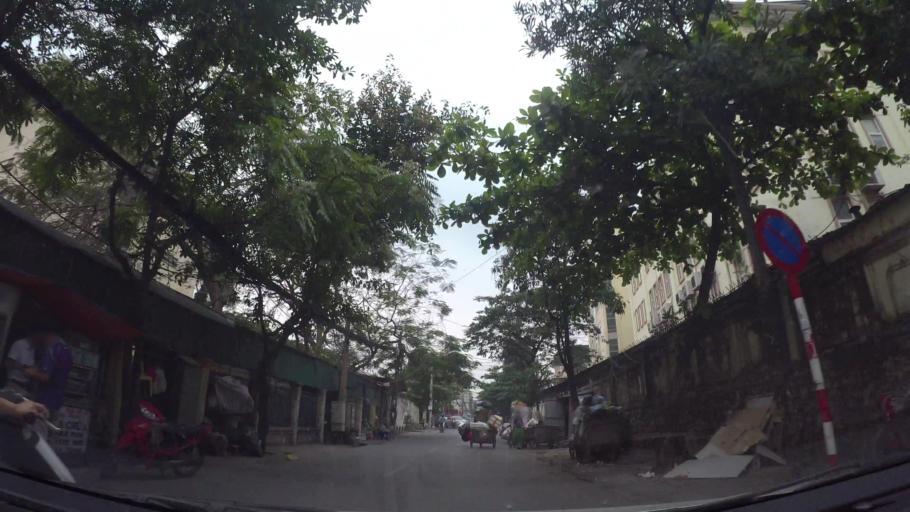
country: VN
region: Ha Noi
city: Cau Dien
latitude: 21.0326
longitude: 105.7789
